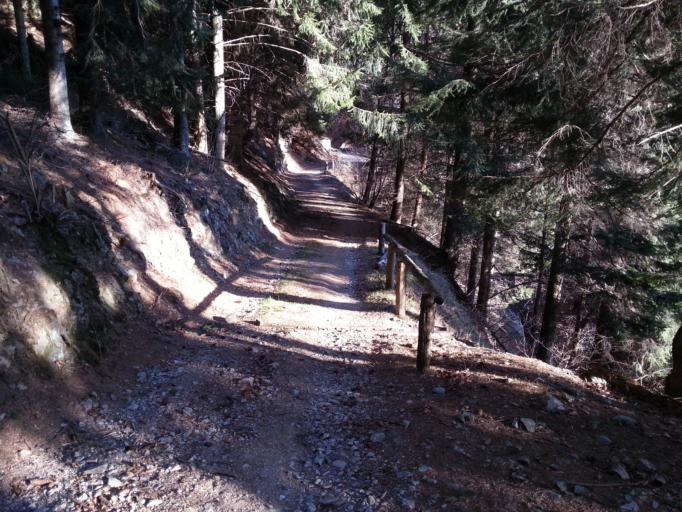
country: CH
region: Ticino
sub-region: Lugano District
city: Gravesano
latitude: 46.0477
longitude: 8.8628
